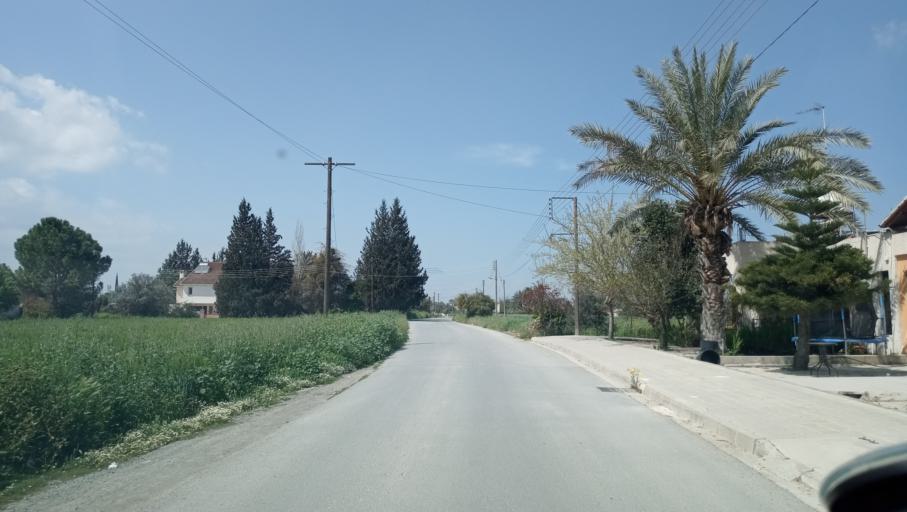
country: CY
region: Lefkosia
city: Dali
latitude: 35.0207
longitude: 33.4182
